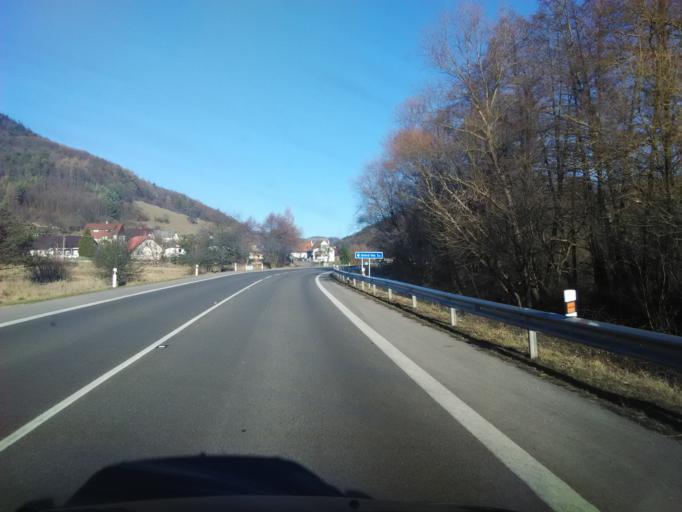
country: SK
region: Banskobystricky
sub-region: Okres Ziar nad Hronom
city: Kremnica
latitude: 48.6604
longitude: 18.9108
